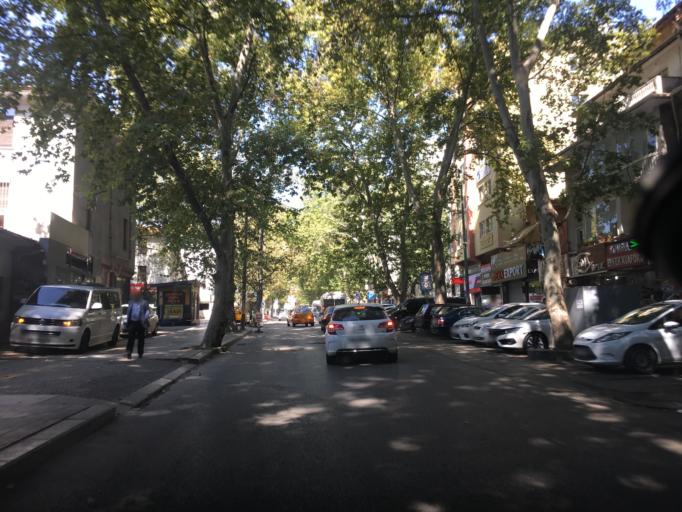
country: TR
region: Ankara
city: Ankara
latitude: 39.9204
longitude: 32.8497
